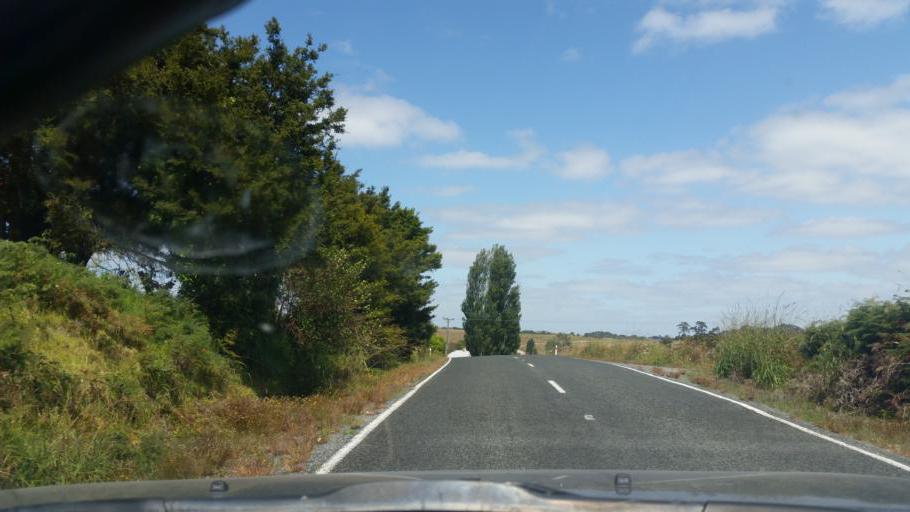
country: NZ
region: Northland
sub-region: Whangarei
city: Ruakaka
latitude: -36.0123
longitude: 174.2918
